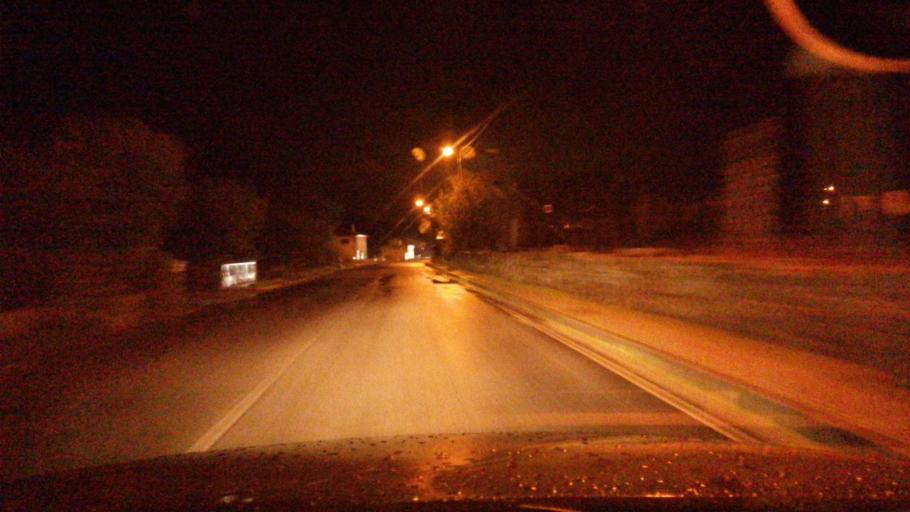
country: PT
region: Viseu
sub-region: Moimenta da Beira
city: Moimenta da Beira
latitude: 40.9375
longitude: -7.5636
